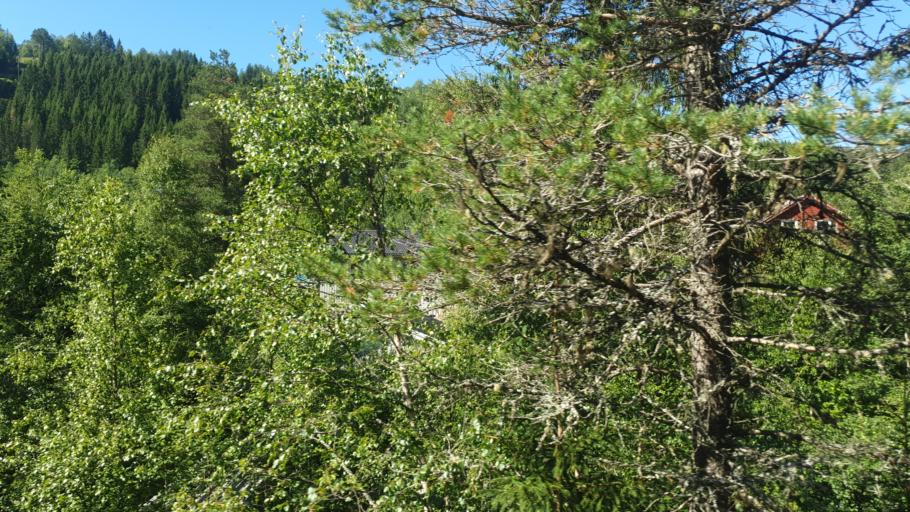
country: NO
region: Sor-Trondelag
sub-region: Meldal
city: Meldal
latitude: 63.1354
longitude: 9.7103
